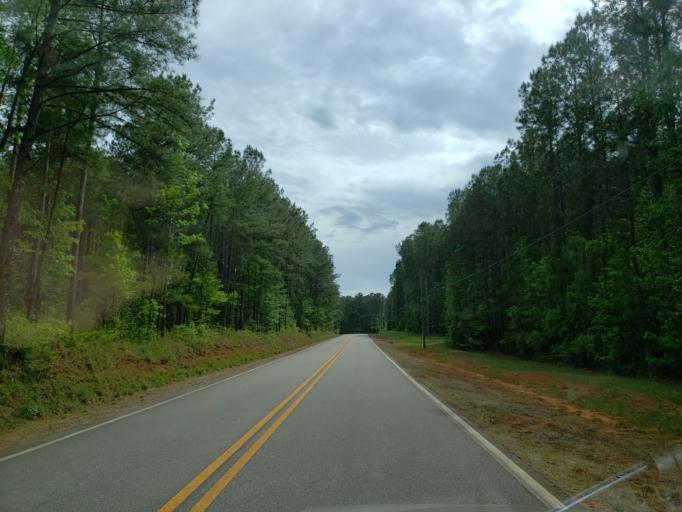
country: US
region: Georgia
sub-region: Monroe County
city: Forsyth
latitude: 32.9430
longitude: -83.9369
